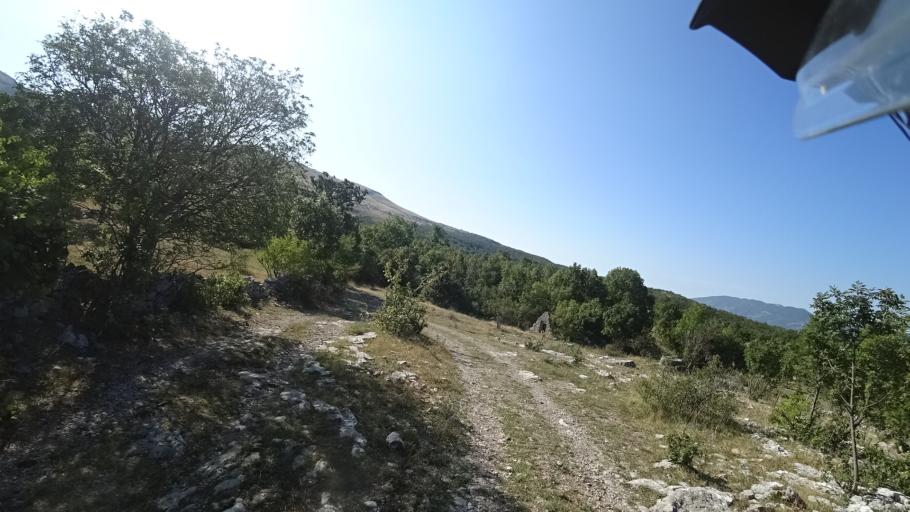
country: HR
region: Sibensko-Kniniska
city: Knin
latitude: 44.2209
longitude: 16.1053
